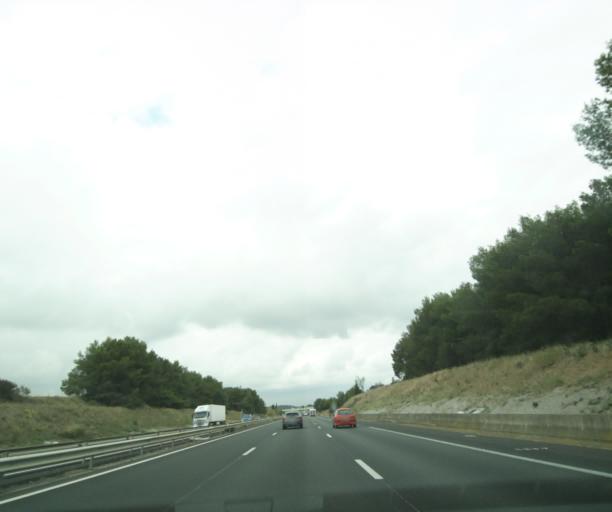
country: FR
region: Languedoc-Roussillon
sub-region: Departement de l'Herault
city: Meze
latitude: 43.4384
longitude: 3.5684
